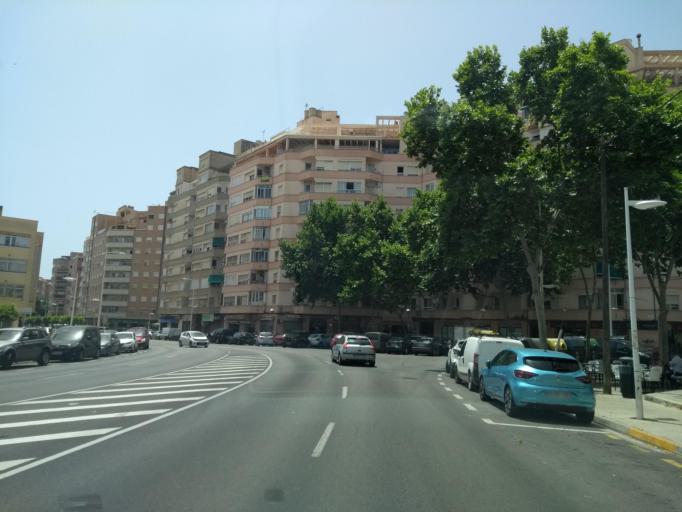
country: ES
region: Balearic Islands
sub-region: Illes Balears
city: Palma
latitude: 39.5863
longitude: 2.6628
